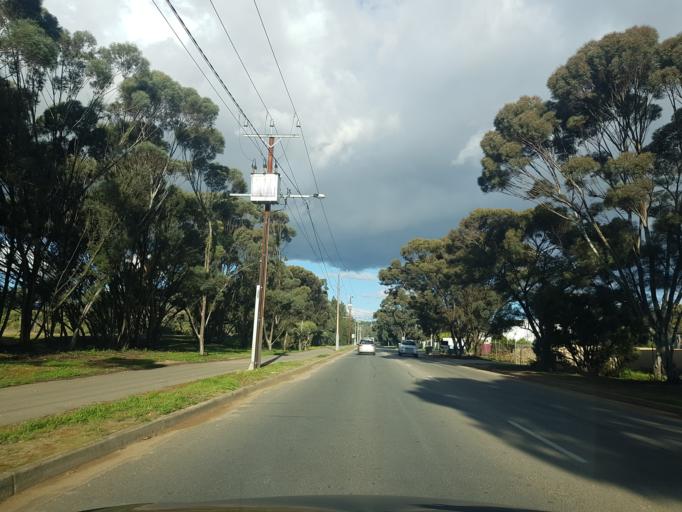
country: AU
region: South Australia
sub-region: Salisbury
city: Ingle Farm
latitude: -34.8116
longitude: 138.6359
